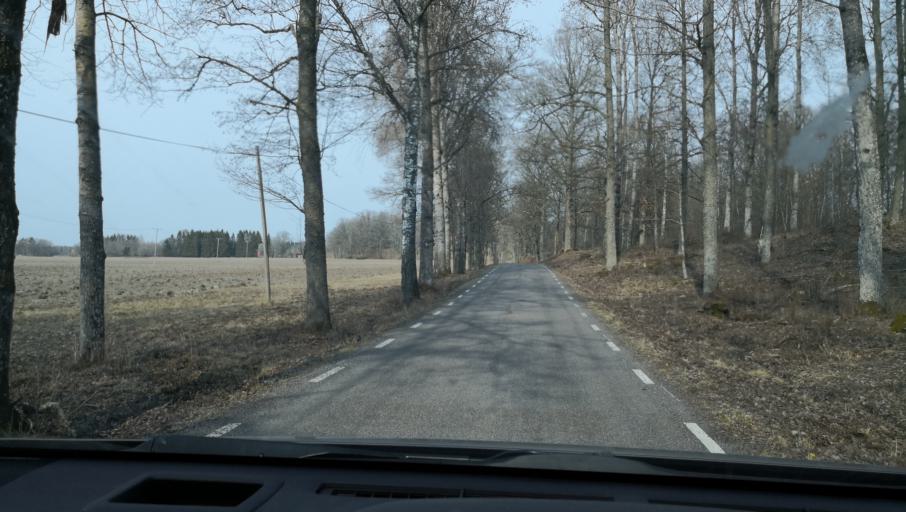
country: SE
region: OErebro
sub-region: Lindesbergs Kommun
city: Frovi
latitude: 59.4007
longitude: 15.4137
